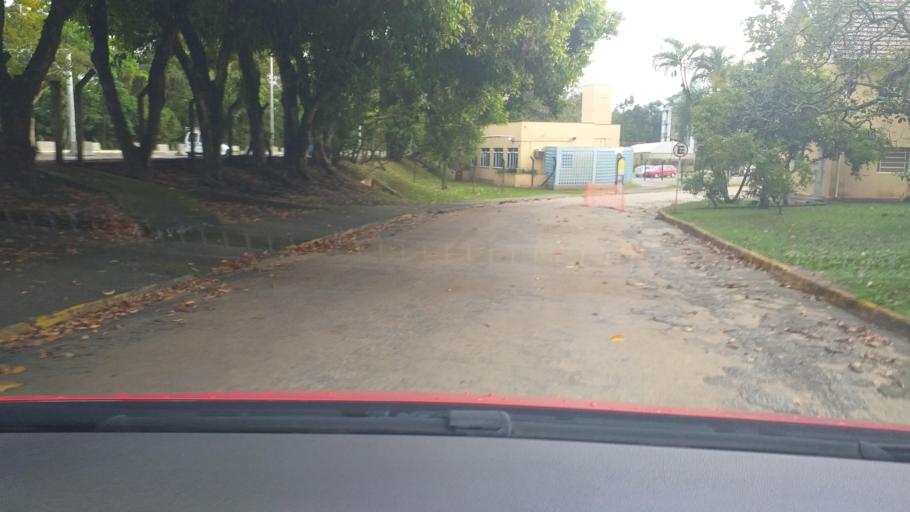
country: BR
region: Santa Catarina
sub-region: Florianopolis
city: Carvoeira
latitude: -27.5994
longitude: -48.5161
